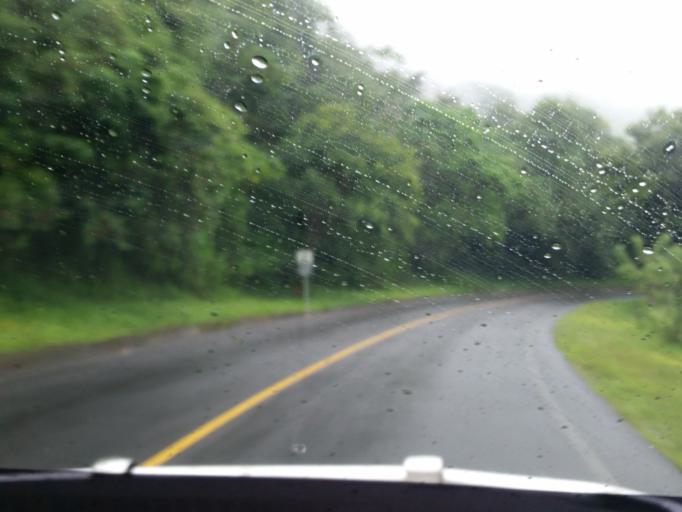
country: NI
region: Matagalpa
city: Matagalpa
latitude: 12.9710
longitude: -85.9196
